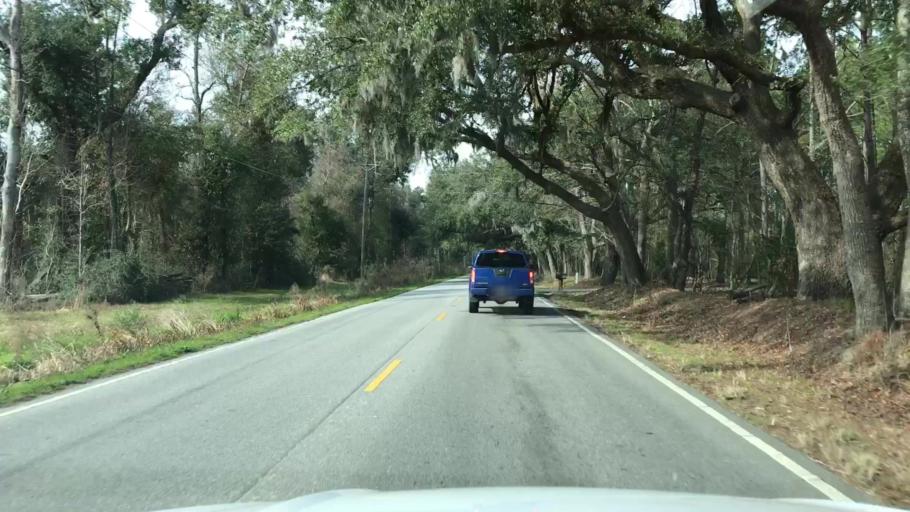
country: US
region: South Carolina
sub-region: Charleston County
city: Shell Point
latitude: 32.7739
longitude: -80.0851
